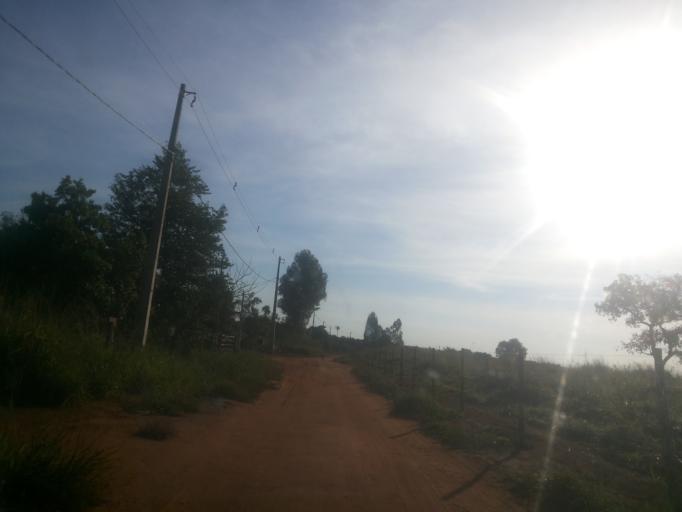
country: BR
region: Minas Gerais
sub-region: Santa Vitoria
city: Santa Vitoria
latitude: -18.9873
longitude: -50.3708
